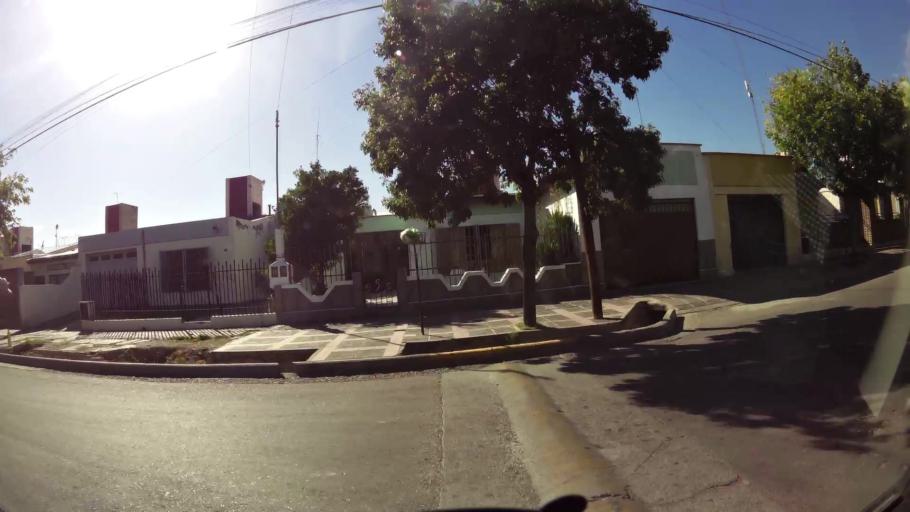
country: AR
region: Mendoza
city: Mendoza
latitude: -32.8786
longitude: -68.8736
